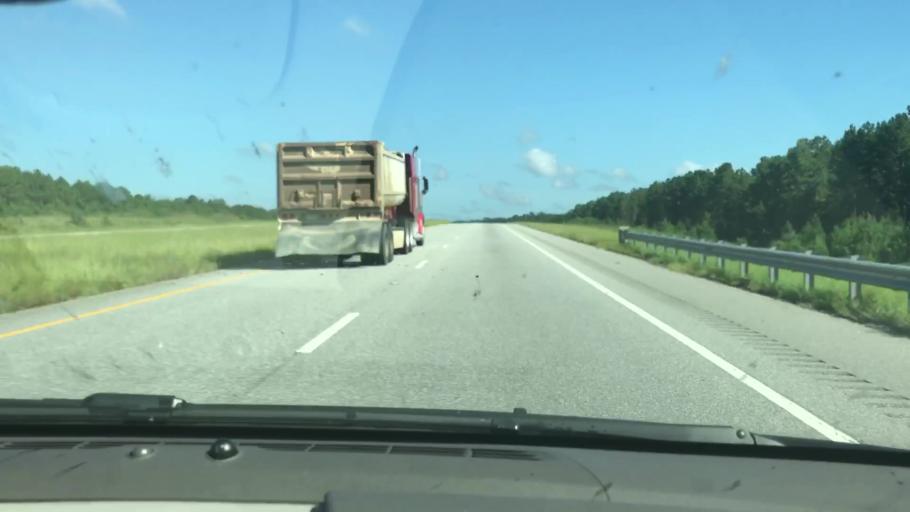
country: US
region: Alabama
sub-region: Barbour County
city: Eufaula
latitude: 32.1195
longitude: -85.1515
